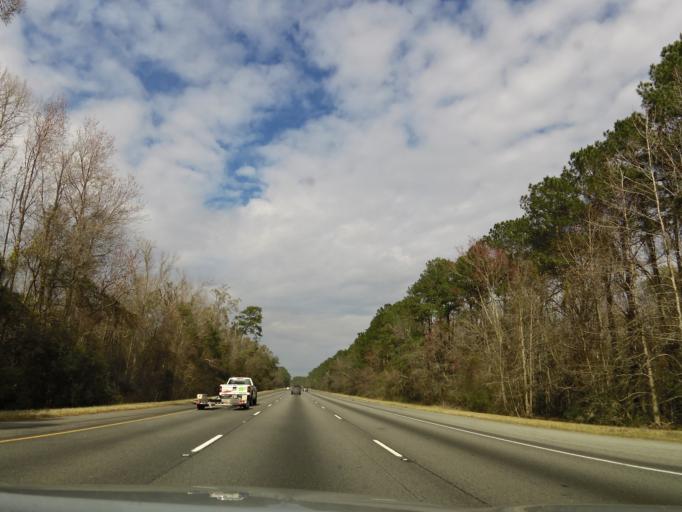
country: US
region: Georgia
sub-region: Bryan County
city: Richmond Hill
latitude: 31.8875
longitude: -81.3269
